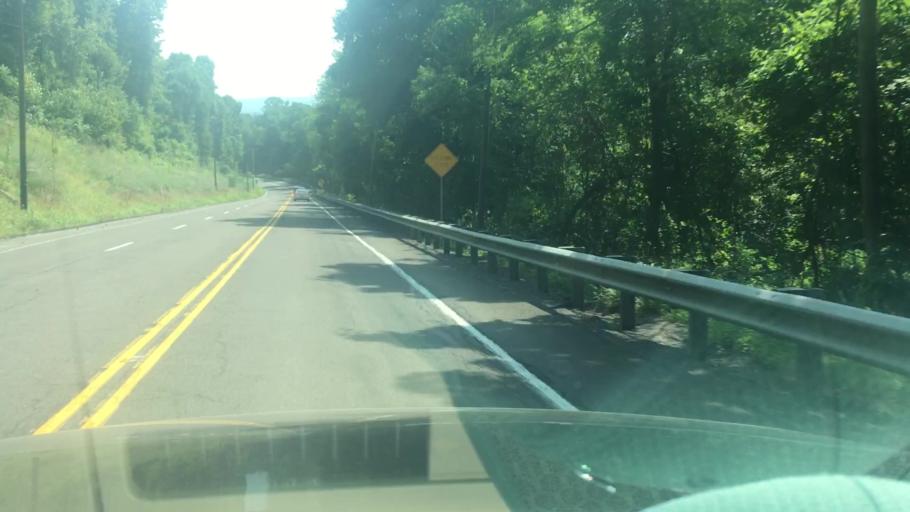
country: US
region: Pennsylvania
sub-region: Schuylkill County
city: Mahanoy City
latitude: 40.8123
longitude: -76.0949
